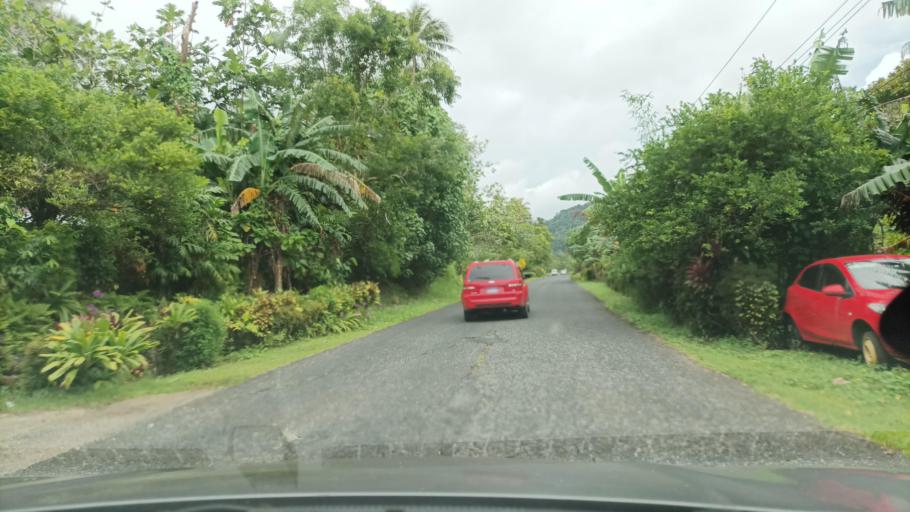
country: FM
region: Pohnpei
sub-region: Kolonia Municipality
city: Kolonia
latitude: 6.9668
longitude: 158.2512
